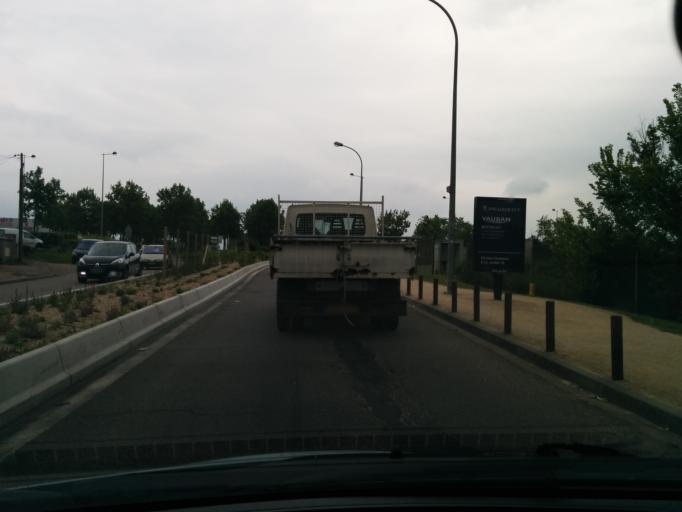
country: FR
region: Ile-de-France
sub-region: Departement des Yvelines
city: Limay
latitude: 48.9918
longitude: 1.7471
